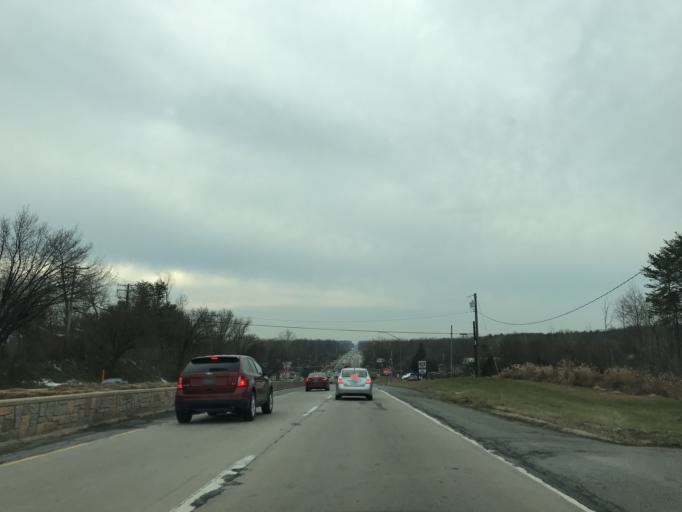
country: US
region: Maryland
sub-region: Harford County
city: Joppatowne
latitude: 39.4249
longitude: -76.3693
